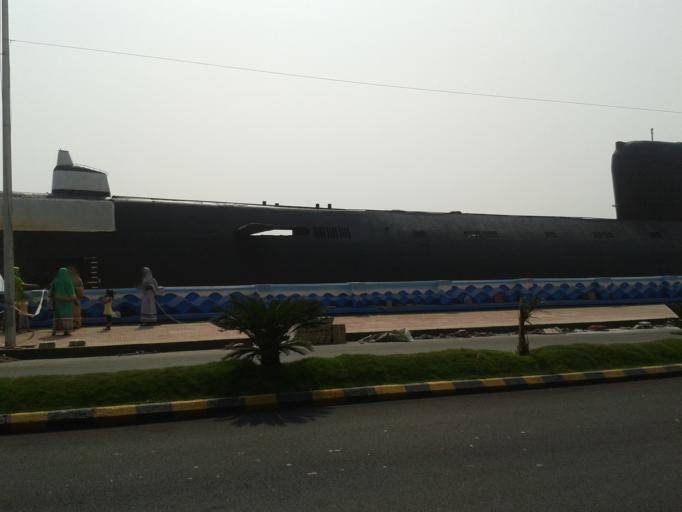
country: IN
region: Andhra Pradesh
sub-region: Vishakhapatnam
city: Yarada
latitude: 17.7176
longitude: 83.3303
